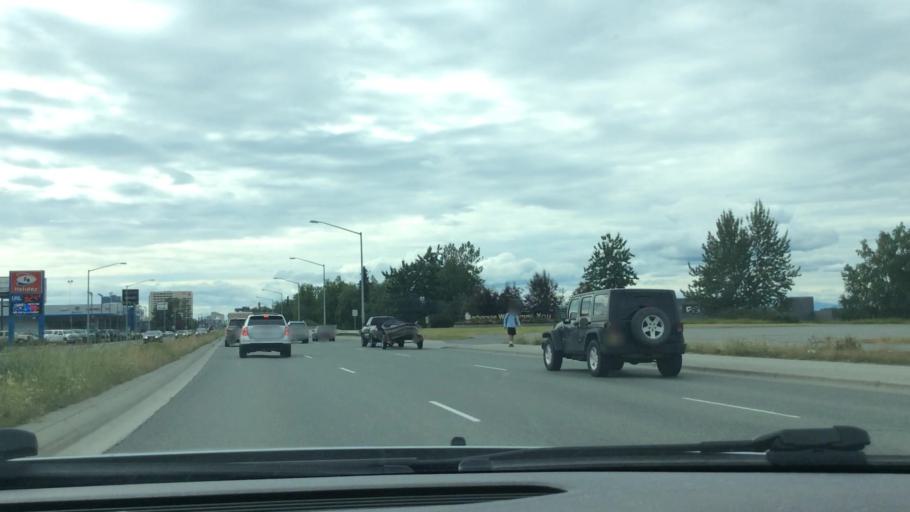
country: US
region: Alaska
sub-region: Anchorage Municipality
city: Anchorage
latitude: 61.2166
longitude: -149.8543
